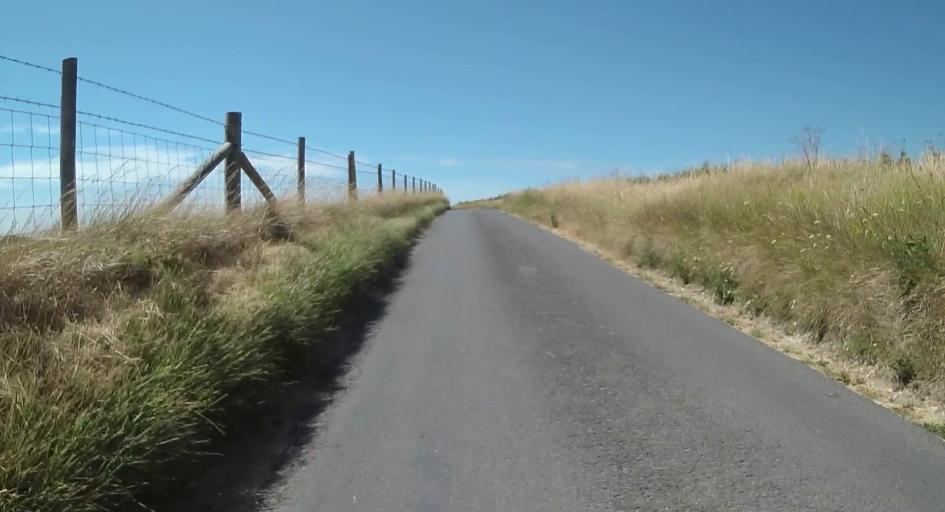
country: GB
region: England
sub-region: Dorset
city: Bovington Camp
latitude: 50.6569
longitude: -2.3007
